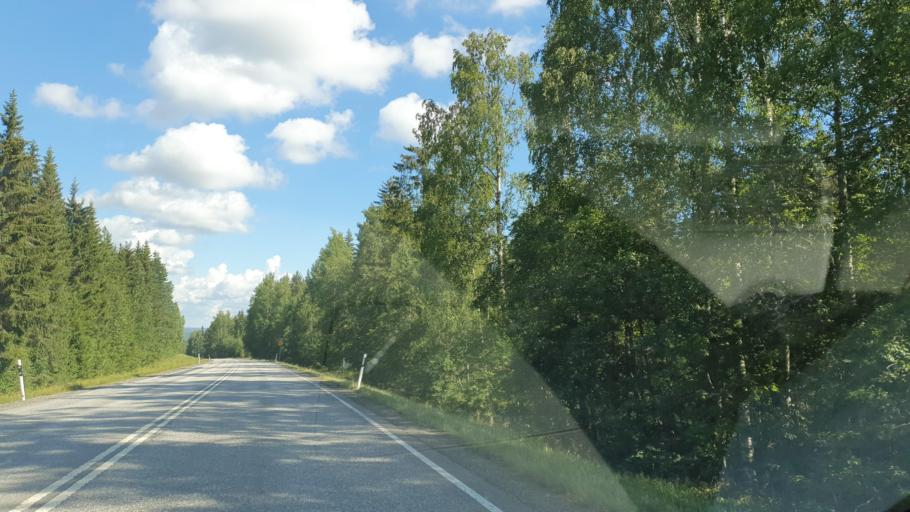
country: FI
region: Northern Savo
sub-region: Ylae-Savo
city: Sonkajaervi
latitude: 63.6836
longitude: 27.3370
